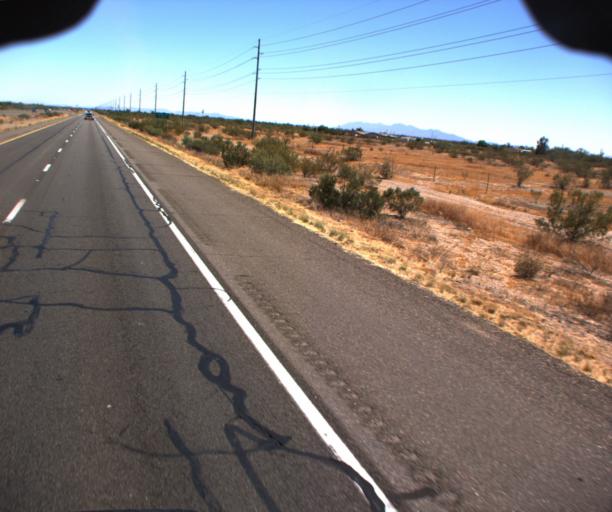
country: US
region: Arizona
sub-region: Maricopa County
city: Sun City West
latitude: 33.7293
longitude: -112.4667
